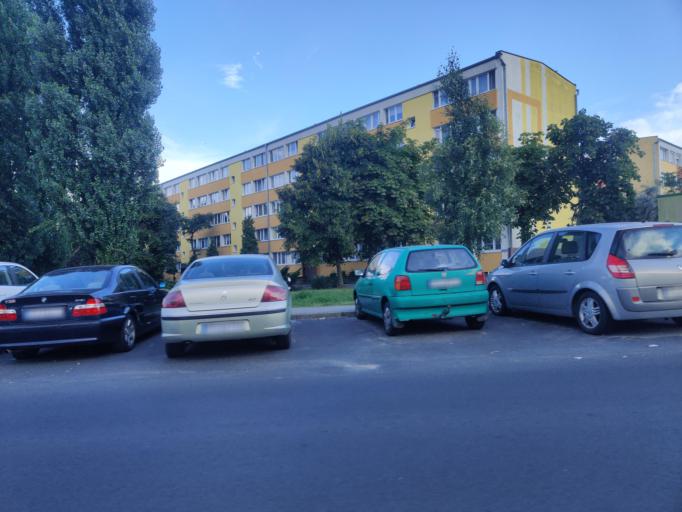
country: PL
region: Greater Poland Voivodeship
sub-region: Konin
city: Konin
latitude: 52.2309
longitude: 18.2755
